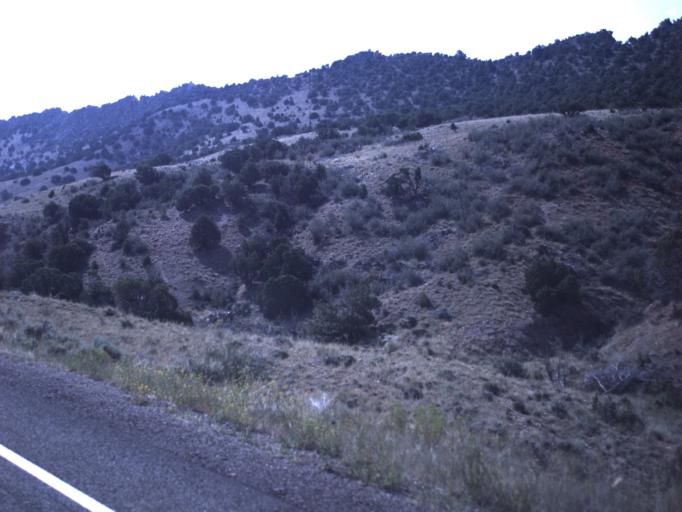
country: US
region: Utah
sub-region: Daggett County
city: Manila
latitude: 40.9323
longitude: -109.7120
